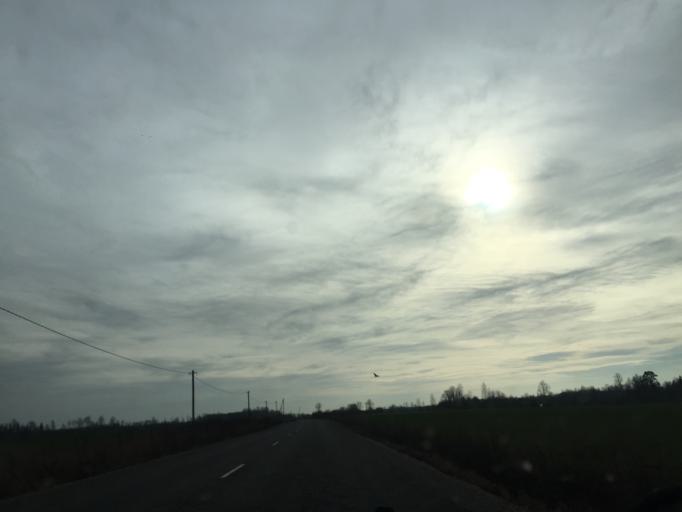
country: LV
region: Talsu Rajons
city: Sabile
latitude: 56.9035
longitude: 22.4004
